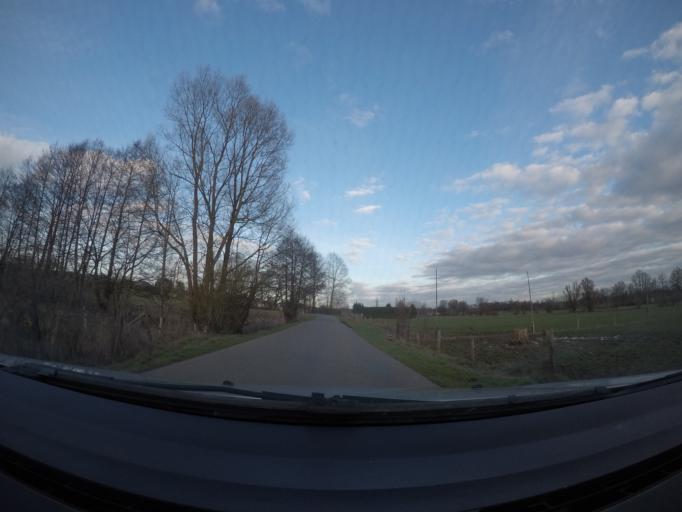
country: BE
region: Wallonia
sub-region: Province du Luxembourg
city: Tintigny
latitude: 49.6993
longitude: 5.5520
